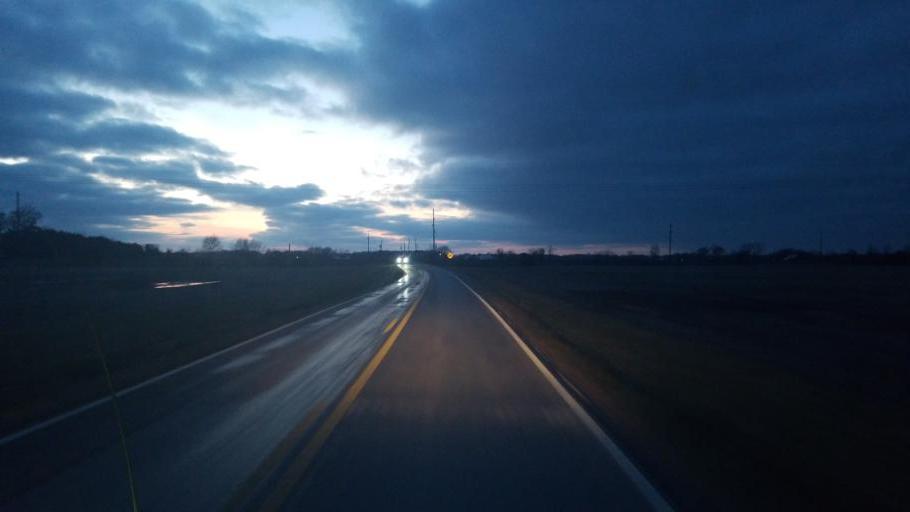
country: US
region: Ohio
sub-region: Marion County
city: Prospect
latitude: 40.4321
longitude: -83.1648
